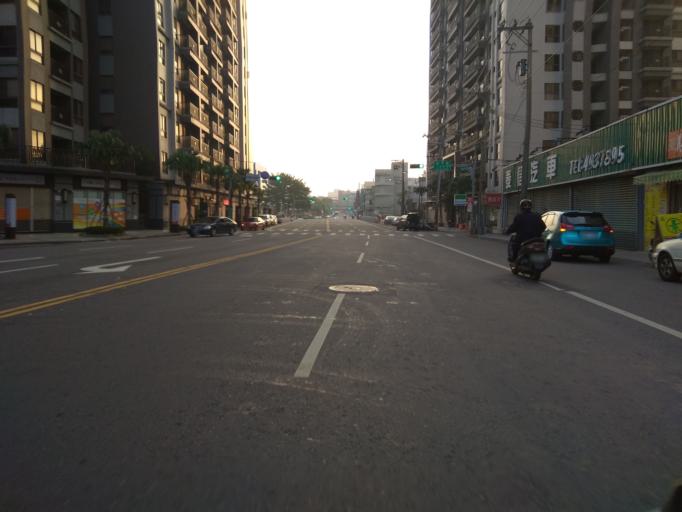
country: TW
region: Taiwan
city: Taoyuan City
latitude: 24.9503
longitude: 121.2136
